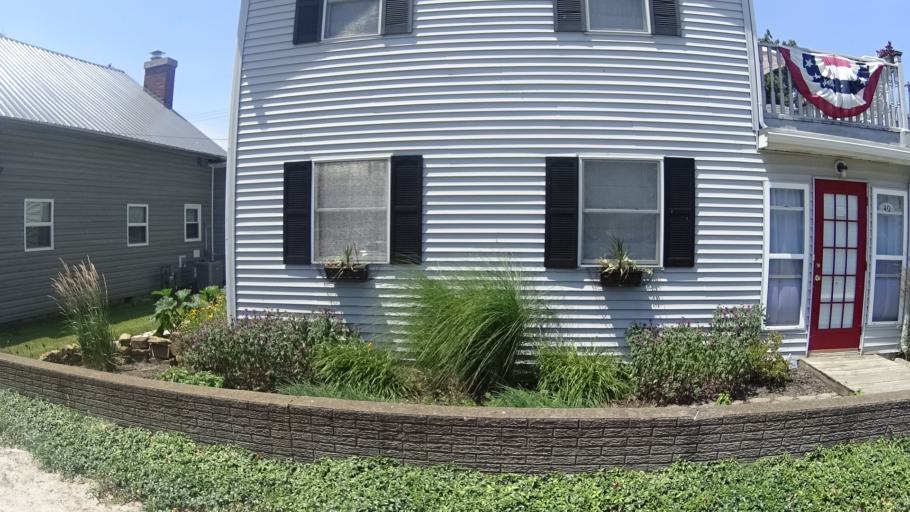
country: US
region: Ohio
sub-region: Erie County
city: Huron
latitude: 41.4121
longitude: -82.5861
